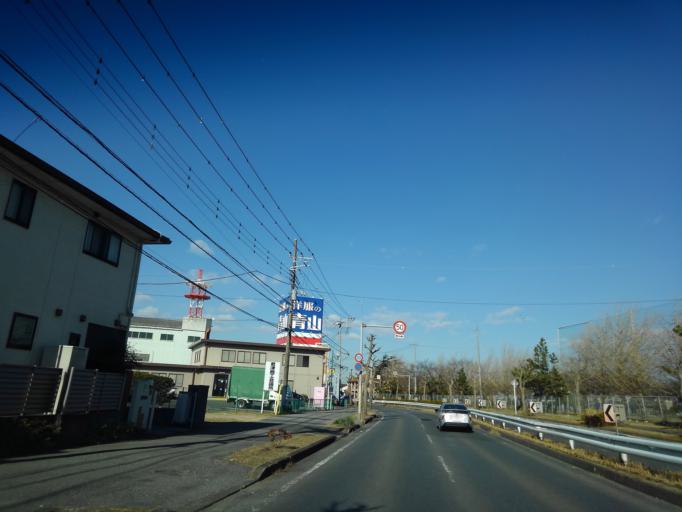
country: JP
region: Chiba
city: Kimitsu
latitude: 35.3248
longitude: 139.9097
